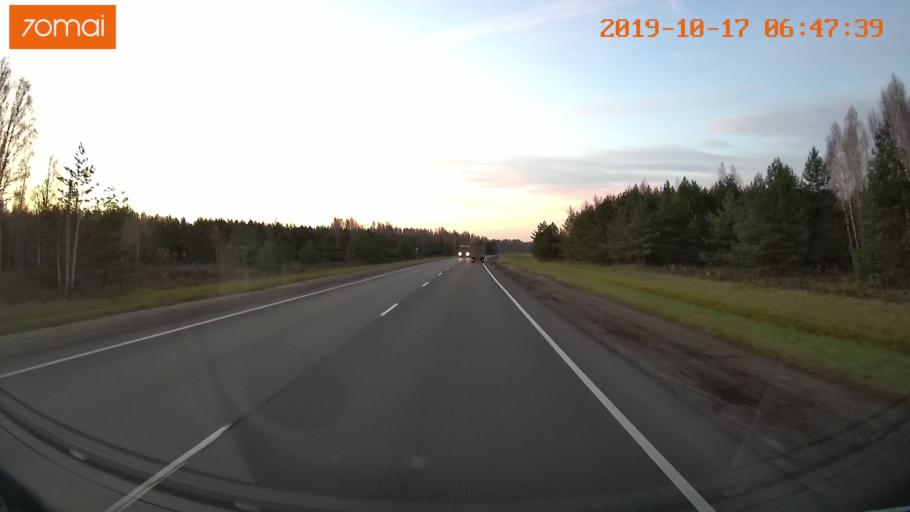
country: RU
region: Vladimir
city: Kideksha
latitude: 56.5330
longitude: 40.5579
